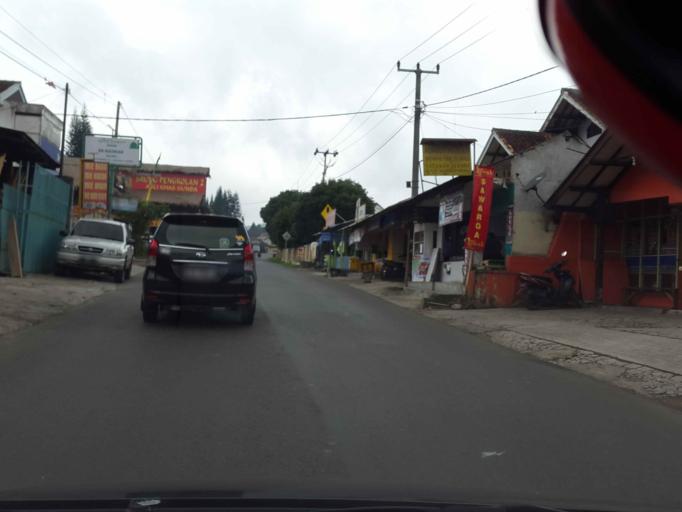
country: ID
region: West Java
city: Lembang
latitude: -6.7976
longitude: 107.6531
